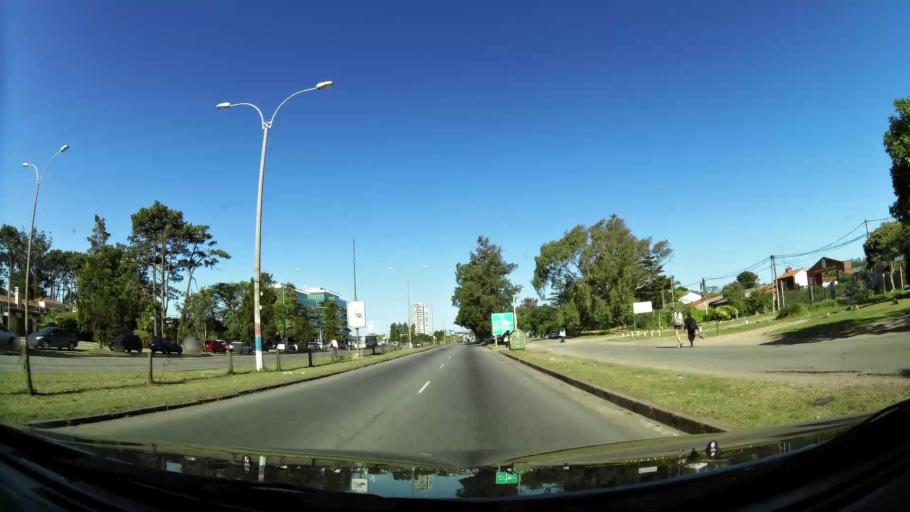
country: UY
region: Canelones
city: Barra de Carrasco
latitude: -34.8759
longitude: -56.0410
